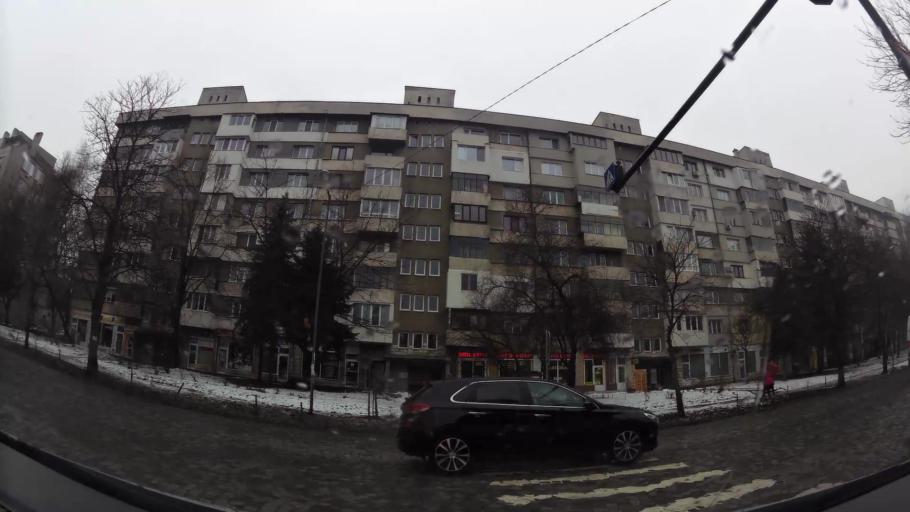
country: BG
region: Sofia-Capital
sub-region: Stolichna Obshtina
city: Sofia
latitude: 42.6741
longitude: 23.2916
